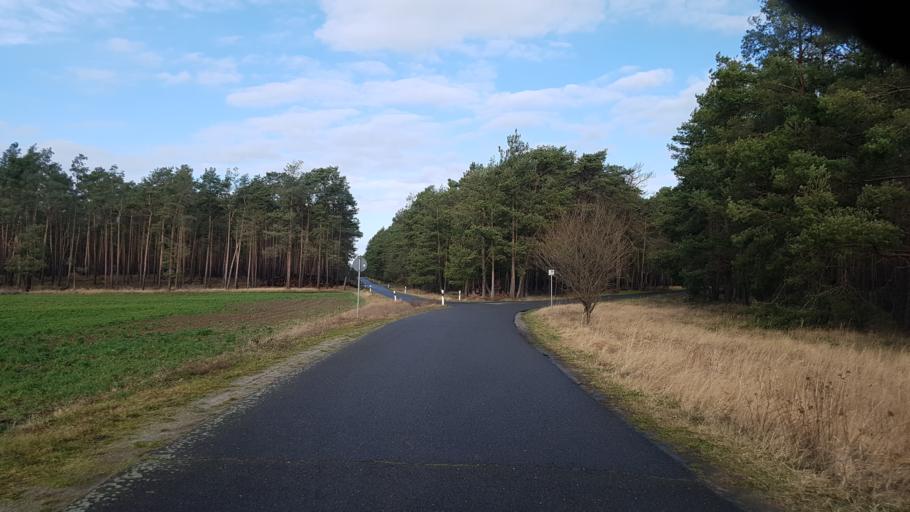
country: DE
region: Brandenburg
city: Schlieben
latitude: 51.7055
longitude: 13.3188
